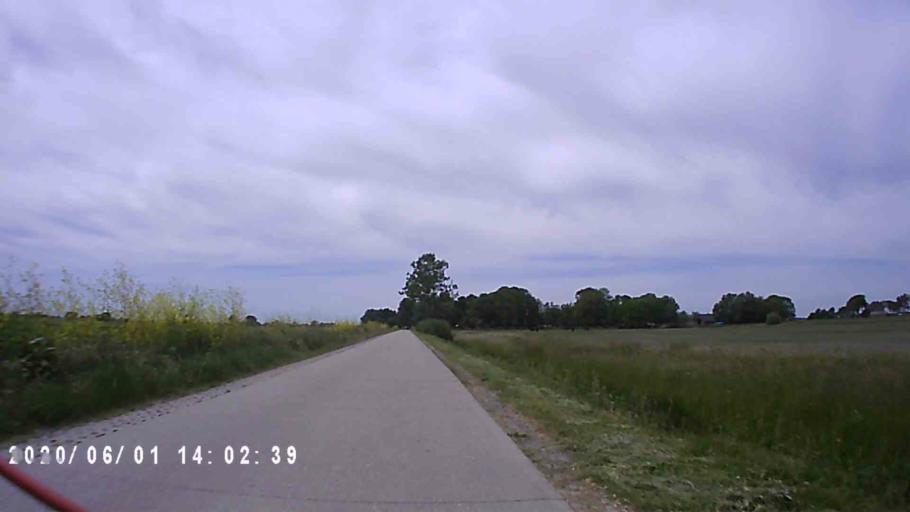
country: NL
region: Friesland
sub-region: Gemeente Littenseradiel
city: Winsum
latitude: 53.1118
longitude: 5.6406
